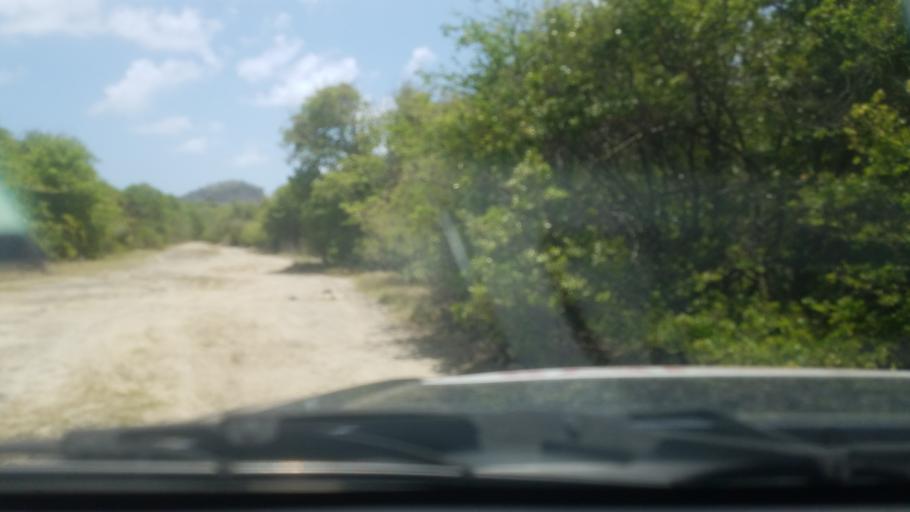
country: LC
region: Vieux-Fort
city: Vieux Fort
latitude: 13.7477
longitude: -60.9356
